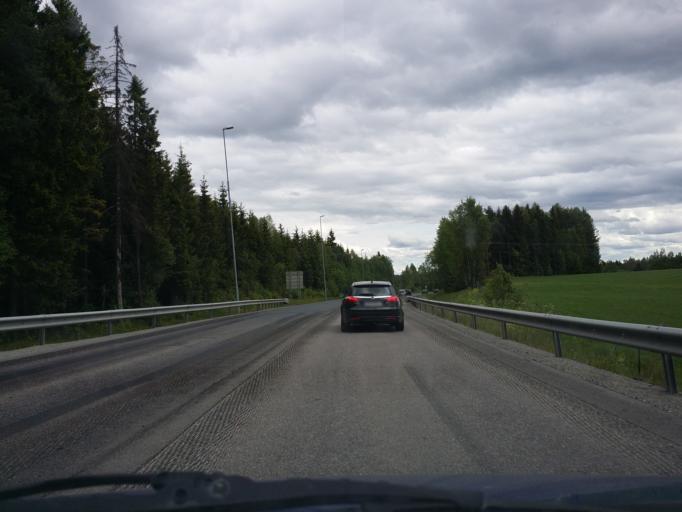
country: NO
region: Hedmark
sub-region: Hamar
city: Hamar
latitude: 60.8409
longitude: 11.0634
